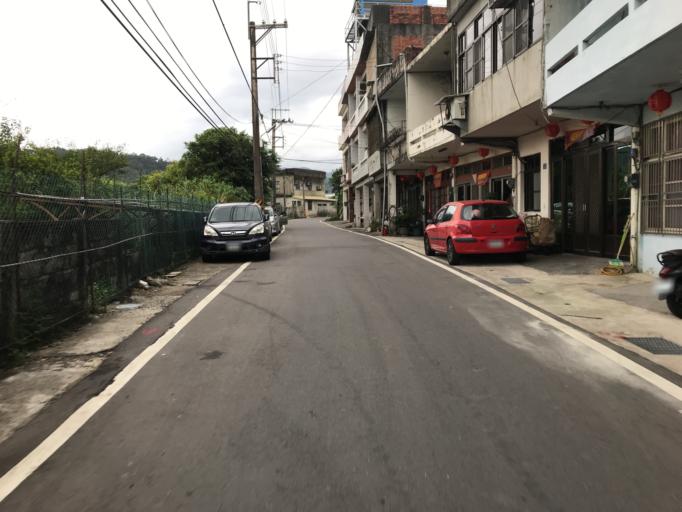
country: TW
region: Taiwan
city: Daxi
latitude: 24.7845
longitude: 121.1753
